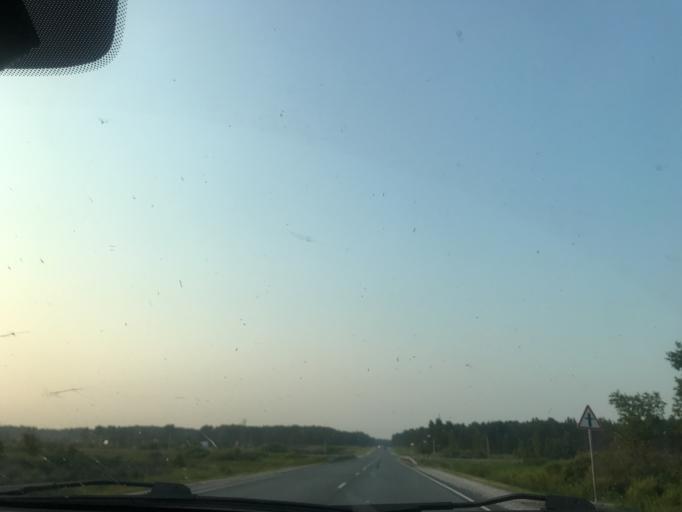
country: RU
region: Novosibirsk
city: Dorogino
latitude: 54.3733
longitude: 83.3043
